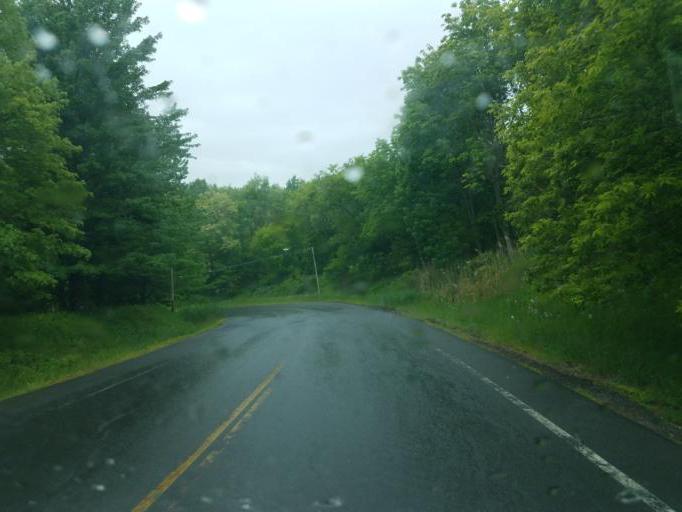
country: US
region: New York
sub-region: Herkimer County
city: Mohawk
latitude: 43.0307
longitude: -75.0051
